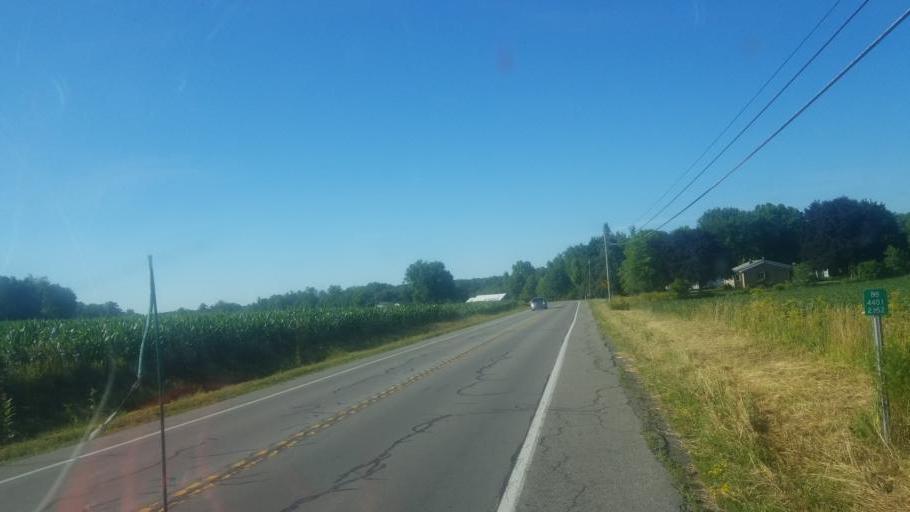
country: US
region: New York
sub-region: Ontario County
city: Phelps
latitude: 42.9912
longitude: -77.0895
